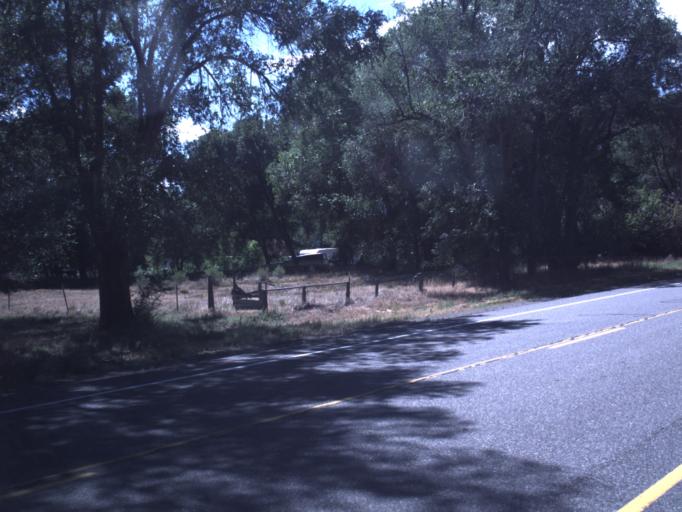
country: US
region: Utah
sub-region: Piute County
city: Junction
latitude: 38.2390
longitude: -112.2200
